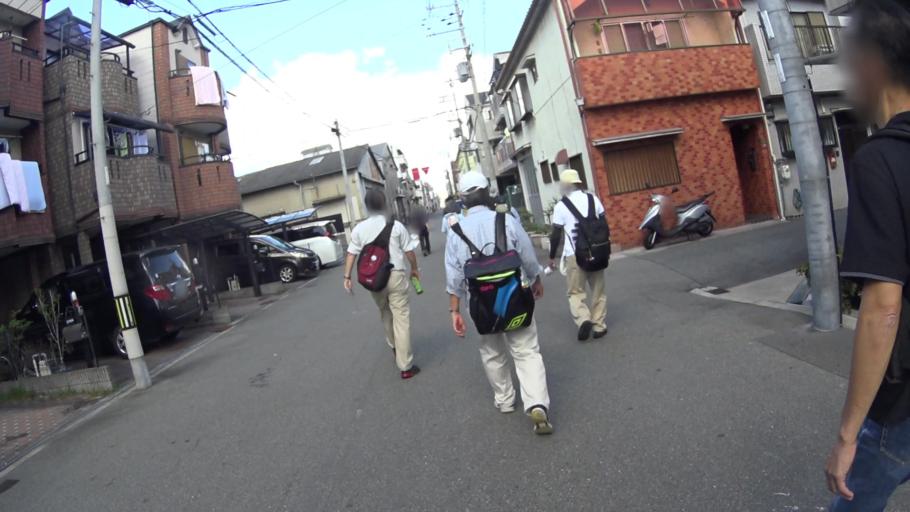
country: JP
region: Osaka
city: Yao
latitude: 34.6443
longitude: 135.5458
